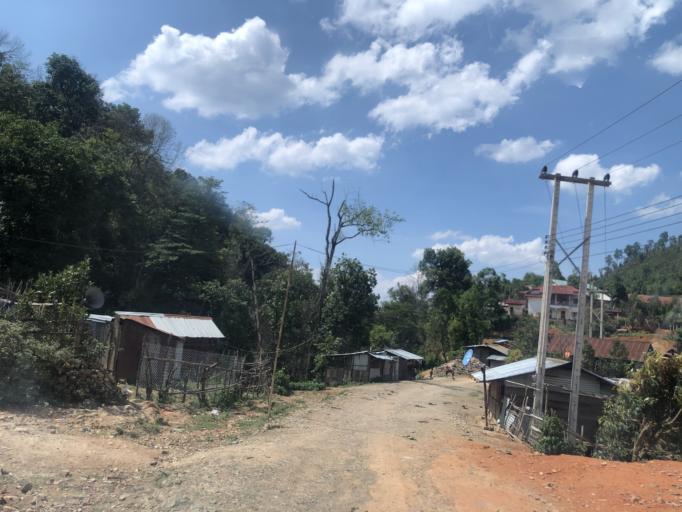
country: LA
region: Phongsali
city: Phongsali
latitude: 21.4143
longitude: 102.2470
